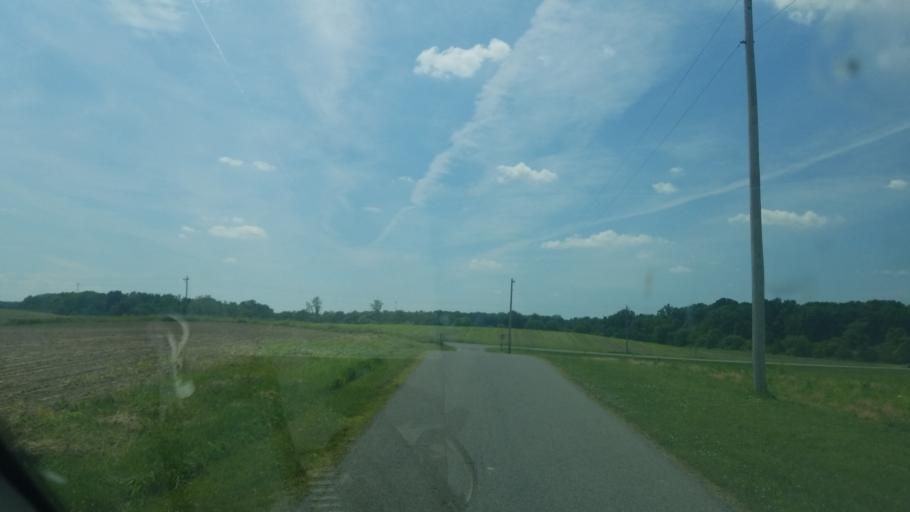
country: US
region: Ohio
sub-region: Hardin County
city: Ada
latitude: 40.6258
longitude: -83.8406
